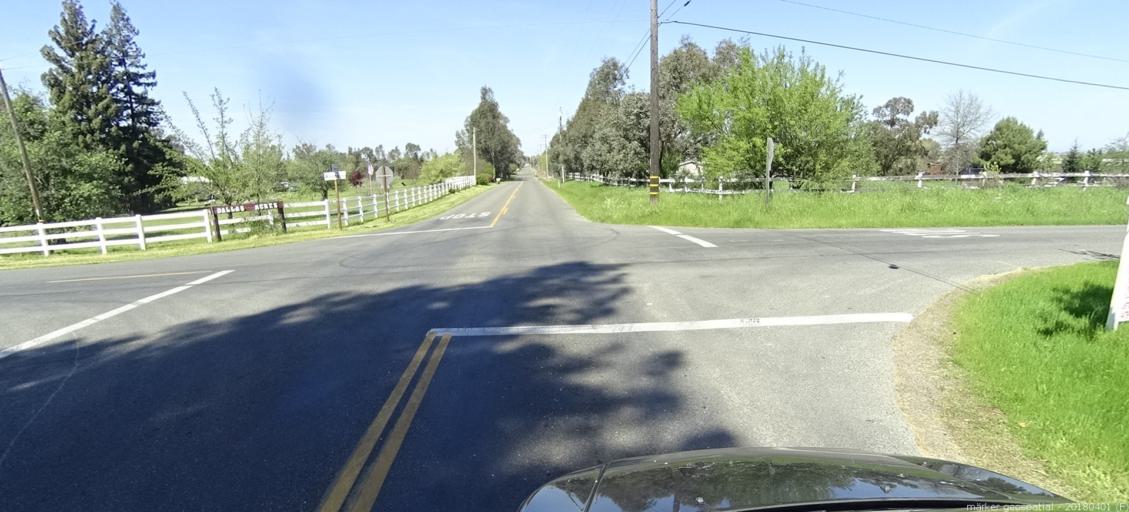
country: US
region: California
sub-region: Sacramento County
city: Wilton
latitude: 38.3940
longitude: -121.2147
